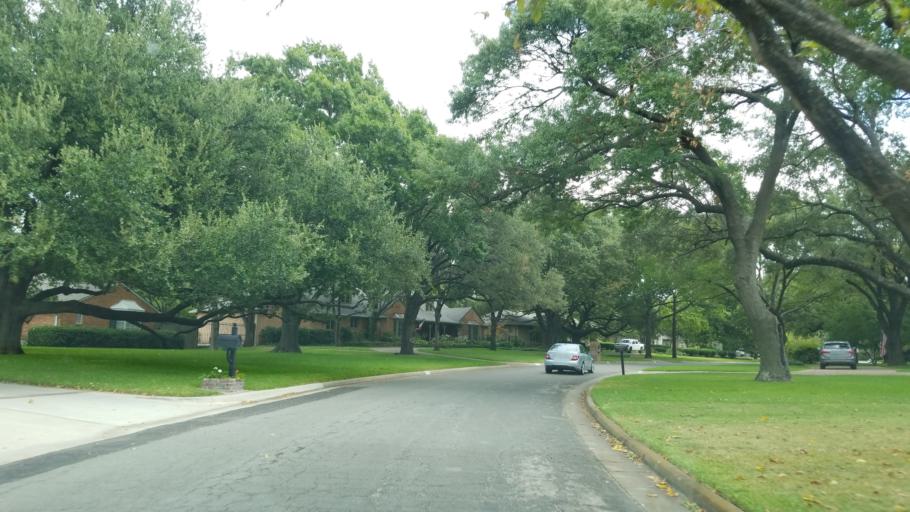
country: US
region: Texas
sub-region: Dallas County
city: Richardson
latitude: 32.9371
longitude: -96.7815
